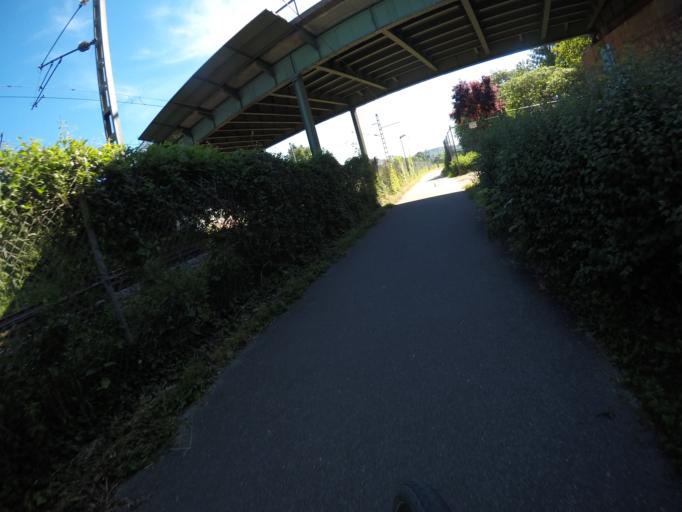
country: DE
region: Baden-Wuerttemberg
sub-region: Karlsruhe Region
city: Weingarten
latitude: 49.0076
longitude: 8.4778
